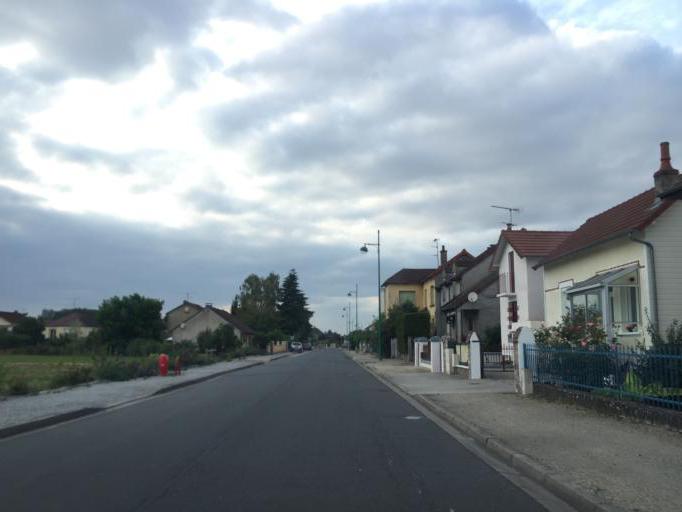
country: FR
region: Auvergne
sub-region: Departement de l'Allier
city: Yzeure
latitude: 46.5577
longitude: 3.3586
